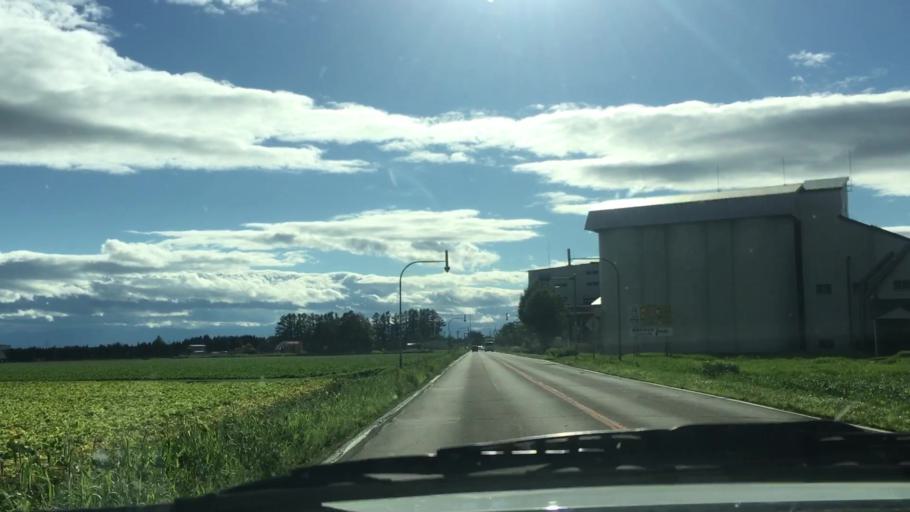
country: JP
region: Hokkaido
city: Otofuke
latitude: 43.1634
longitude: 143.2558
